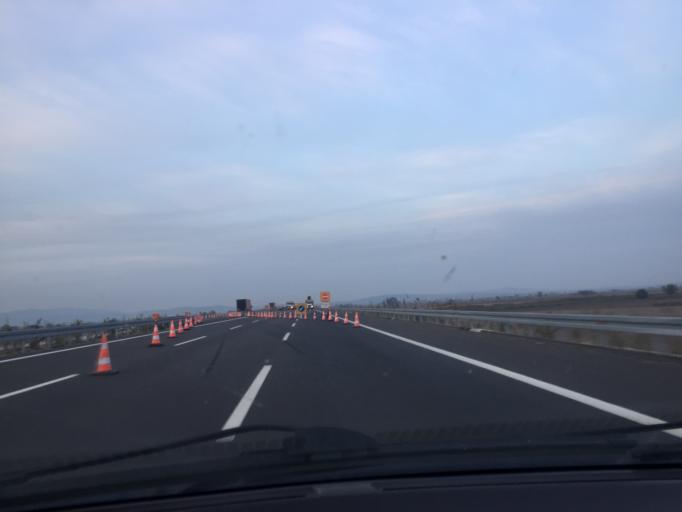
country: TR
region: Manisa
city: Halitpasa
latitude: 38.7218
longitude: 27.6522
